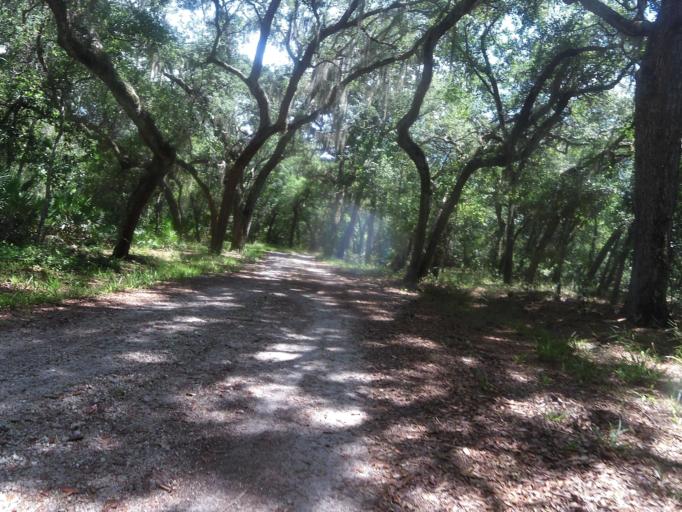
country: US
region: Florida
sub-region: Saint Johns County
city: Villano Beach
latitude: 30.0339
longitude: -81.3363
